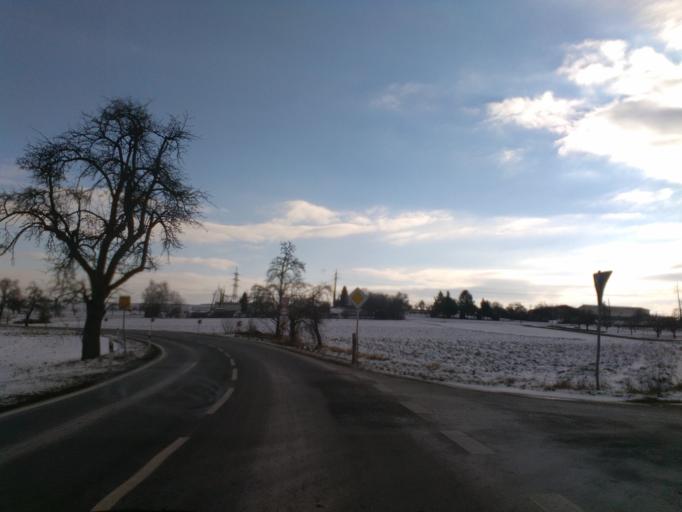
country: DE
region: Baden-Wuerttemberg
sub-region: Regierungsbezirk Stuttgart
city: Filderstadt
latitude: 48.6681
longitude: 9.2441
